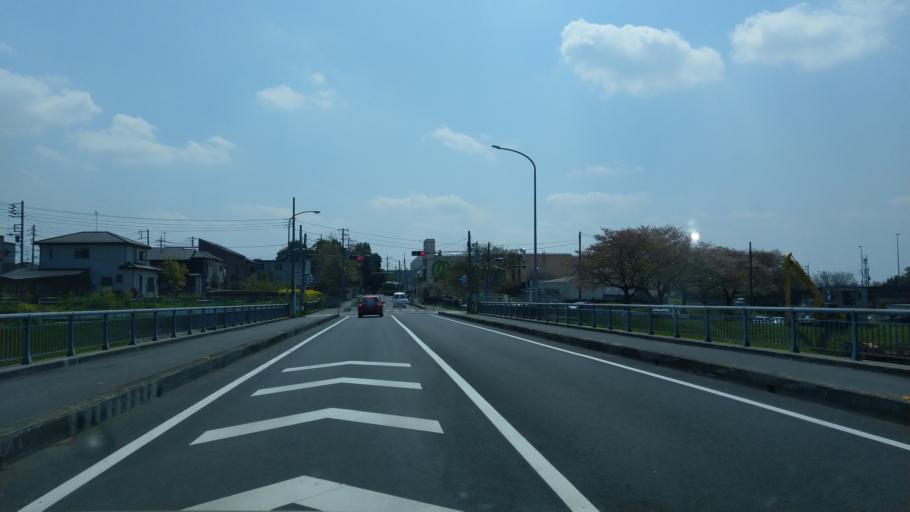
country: JP
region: Saitama
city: Saitama
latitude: 35.8948
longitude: 139.6651
